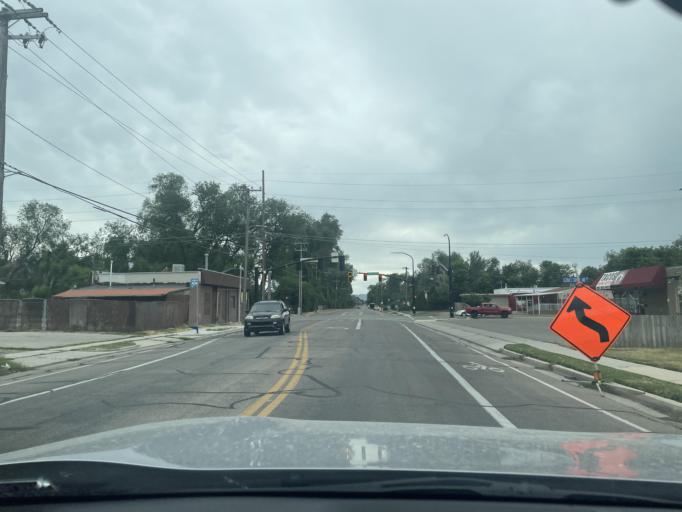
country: US
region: Utah
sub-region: Salt Lake County
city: South Salt Lake
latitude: 40.7133
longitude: -111.8769
